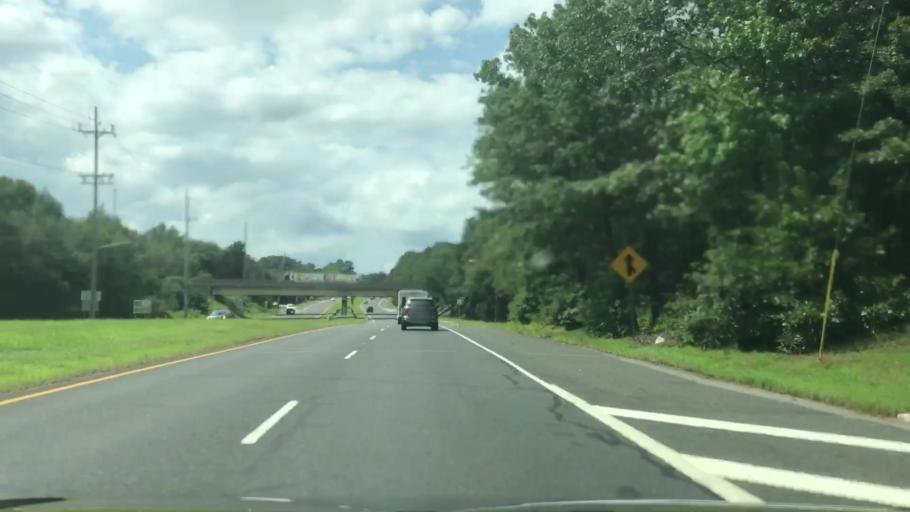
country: US
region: New Jersey
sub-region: Monmouth County
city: Wanamassa
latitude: 40.2282
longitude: -74.0477
